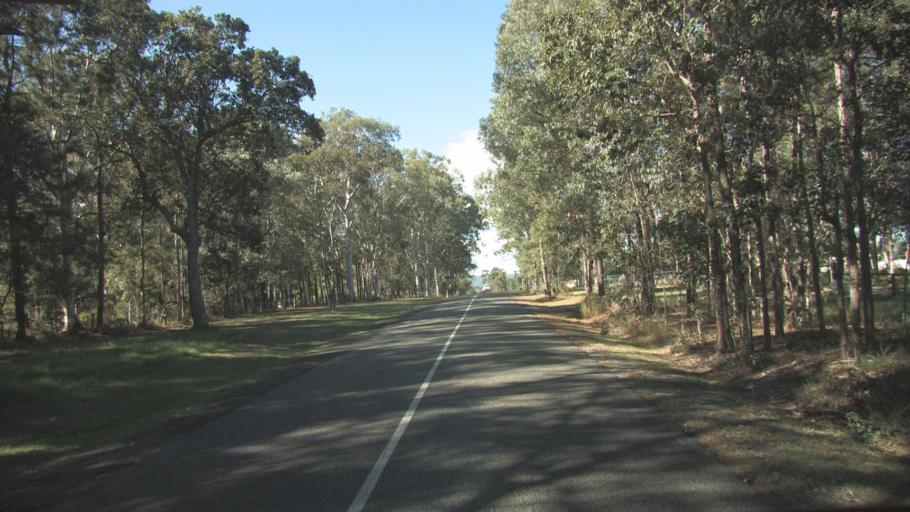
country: AU
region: Queensland
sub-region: Logan
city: Chambers Flat
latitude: -27.7918
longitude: 153.0797
